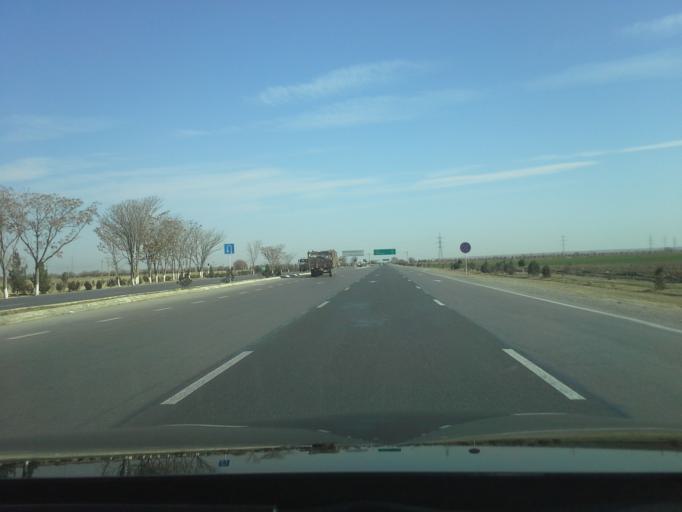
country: TM
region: Ahal
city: Annau
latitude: 37.9053
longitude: 58.5359
